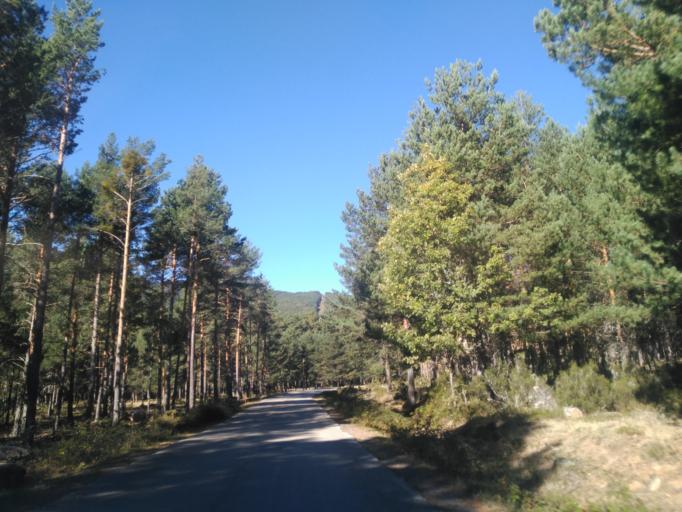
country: ES
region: Castille and Leon
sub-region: Provincia de Soria
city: Vinuesa
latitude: 41.9755
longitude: -2.7894
